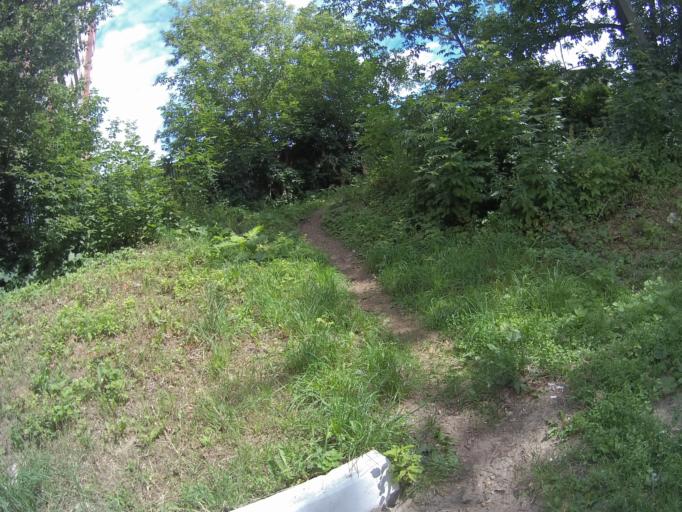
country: RU
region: Vladimir
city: Vladimir
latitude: 56.1232
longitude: 40.3810
